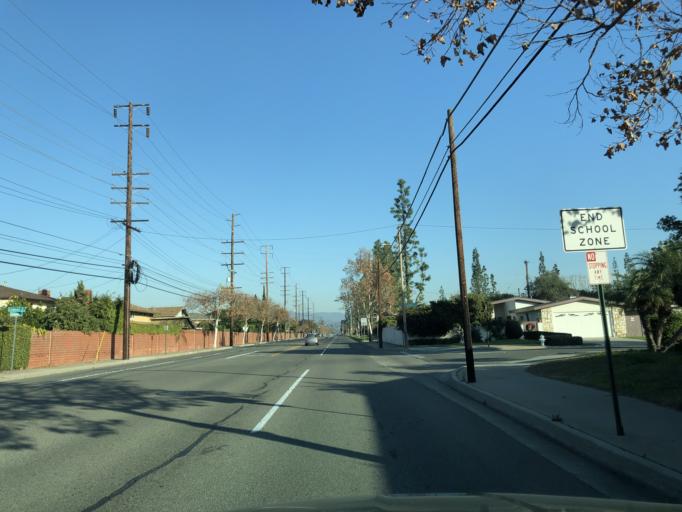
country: US
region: California
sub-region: Orange County
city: Orange
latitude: 33.7732
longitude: -117.8486
